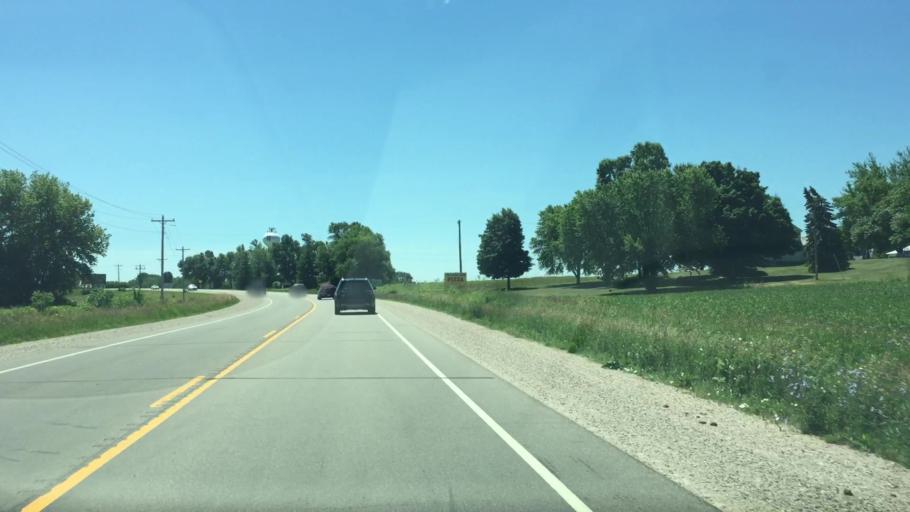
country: US
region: Wisconsin
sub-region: Calumet County
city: New Holstein
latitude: 43.9633
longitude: -88.1124
